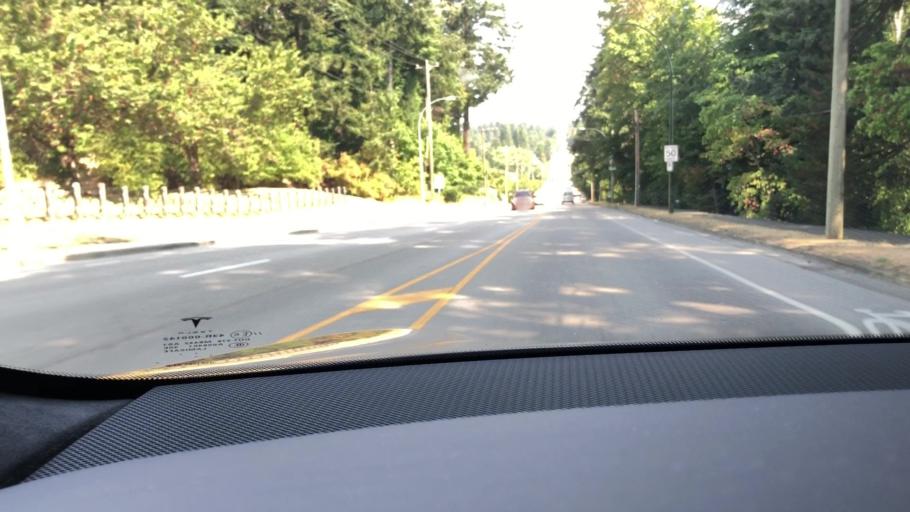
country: US
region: Washington
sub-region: Whatcom County
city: Point Roberts
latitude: 49.0050
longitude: -123.0687
